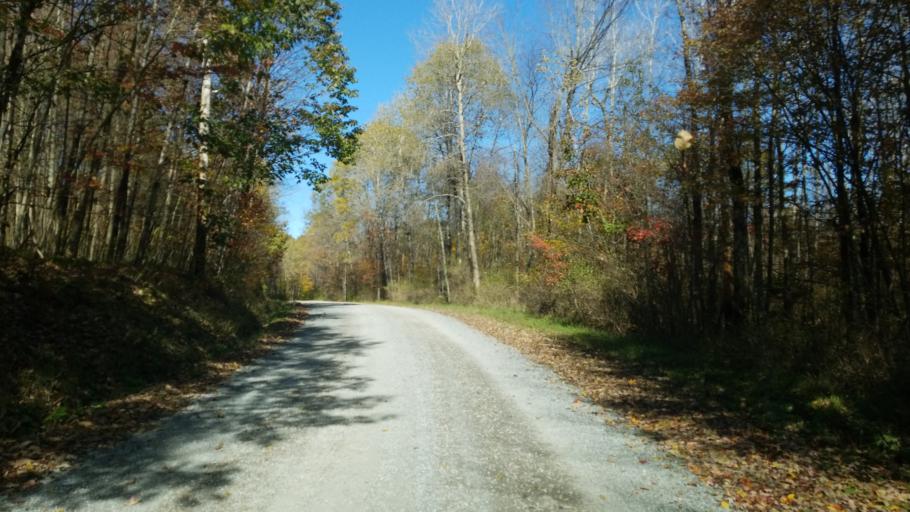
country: US
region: Pennsylvania
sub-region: Jefferson County
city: Falls Creek
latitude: 41.1768
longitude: -78.7838
